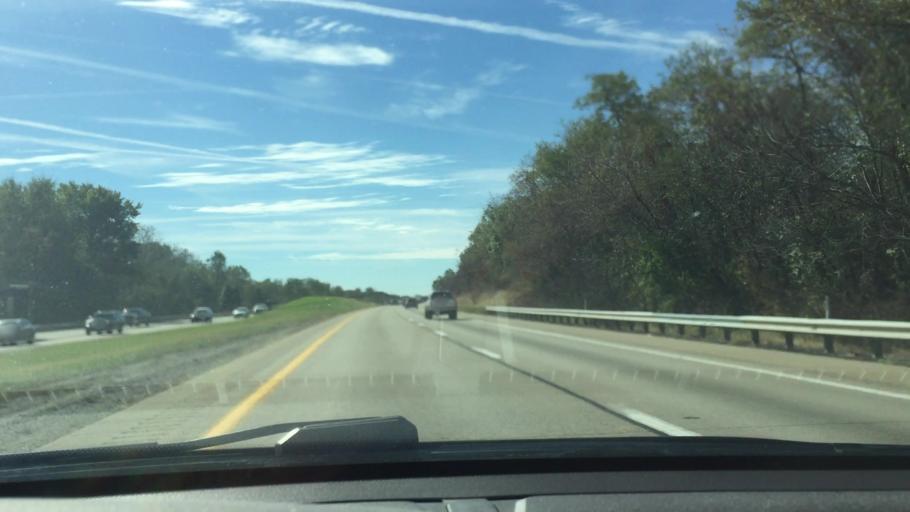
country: US
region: Pennsylvania
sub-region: Washington County
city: Cecil-Bishop
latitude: 40.3209
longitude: -80.1462
